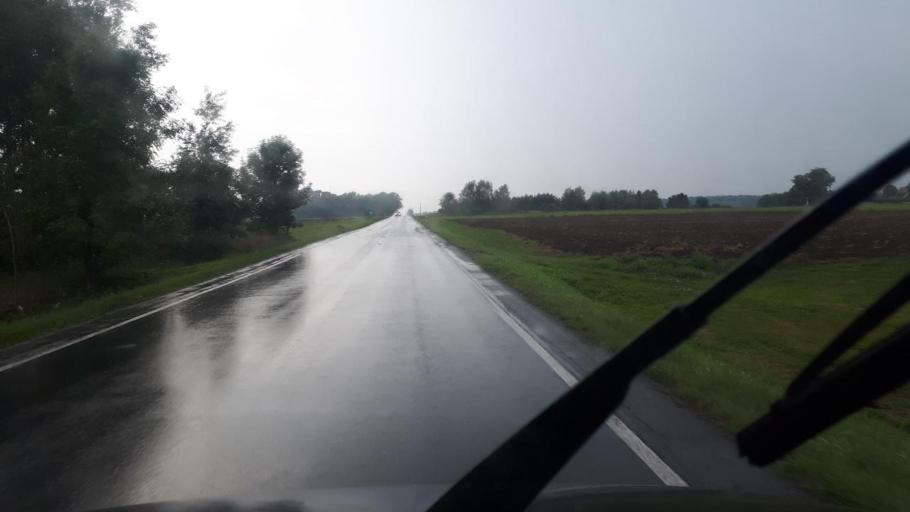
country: PL
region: Silesian Voivodeship
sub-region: Powiat gliwicki
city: Wielowies
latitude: 50.5283
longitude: 18.6469
